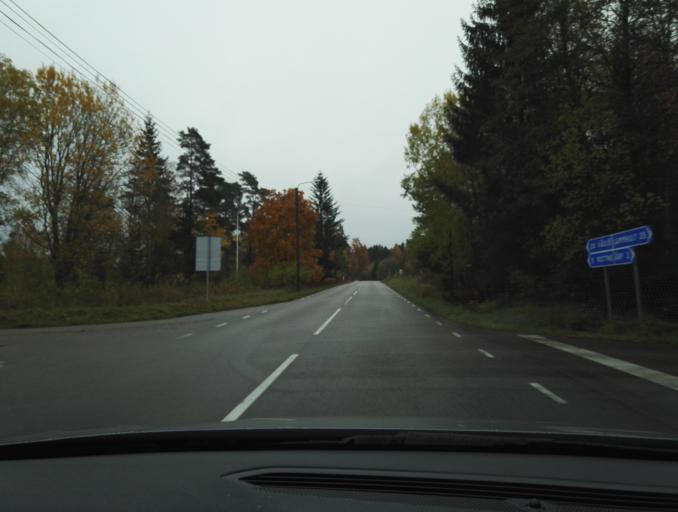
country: SE
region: Kronoberg
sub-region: Vaxjo Kommun
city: Rottne
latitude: 57.0298
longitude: 14.8167
